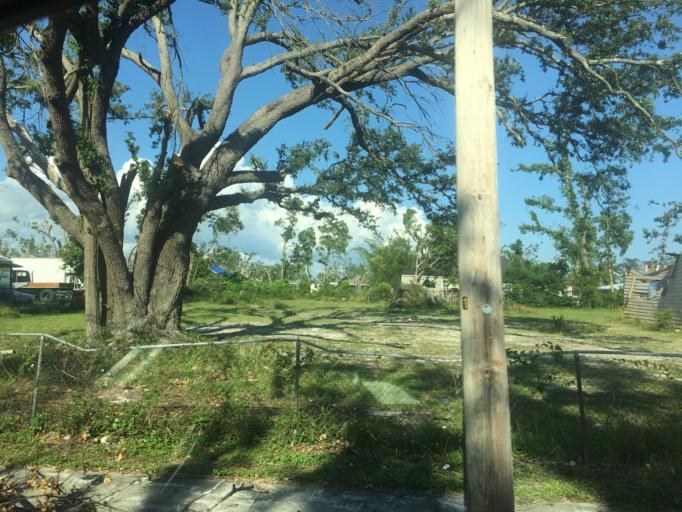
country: US
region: Florida
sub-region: Bay County
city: Cedar Grove
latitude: 30.1598
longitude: -85.6334
